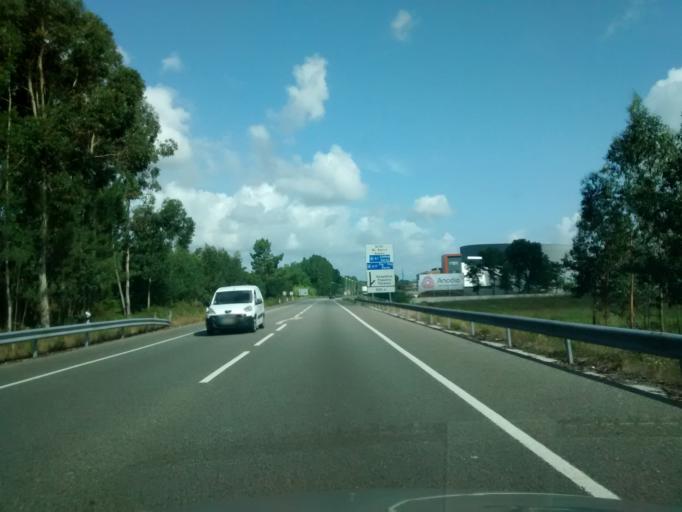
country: PT
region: Aveiro
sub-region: Anadia
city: Sangalhos
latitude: 40.4766
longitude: -8.4747
